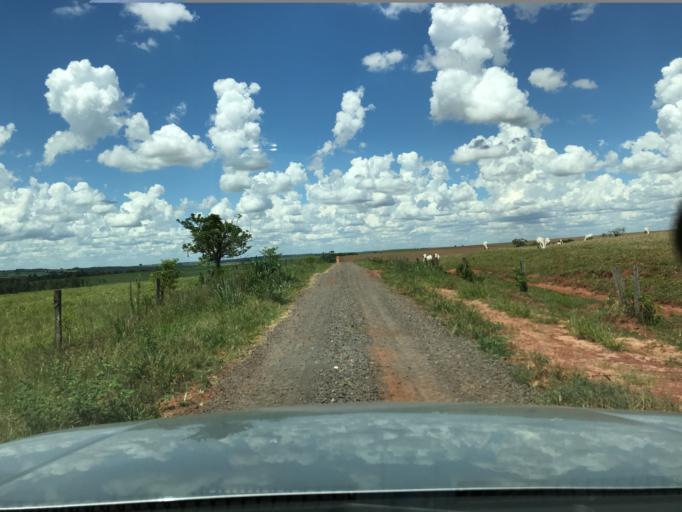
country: BR
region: Parana
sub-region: Palotina
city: Palotina
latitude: -24.1780
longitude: -53.7756
